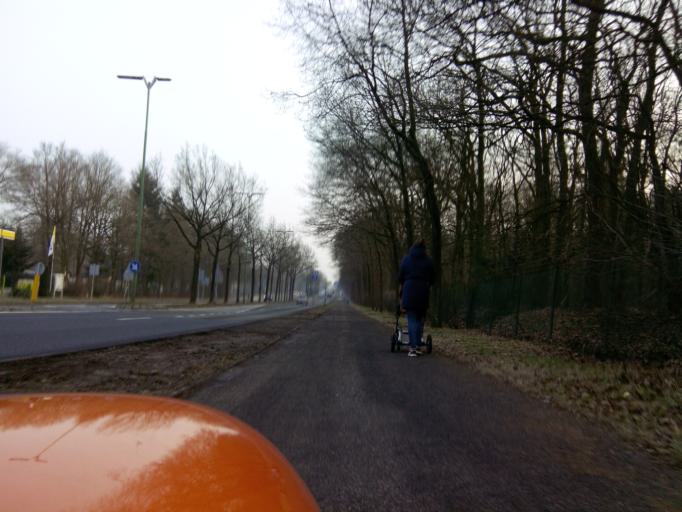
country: NL
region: Utrecht
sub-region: Gemeente Zeist
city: Zeist
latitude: 52.1073
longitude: 5.2368
